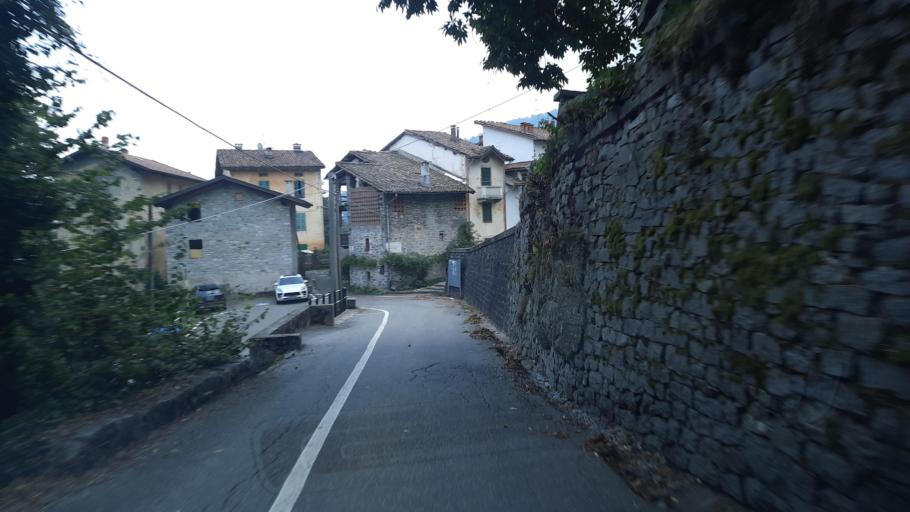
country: IT
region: Piedmont
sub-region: Provincia di Biella
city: San Paolo Cervo
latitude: 45.6553
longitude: 8.0032
